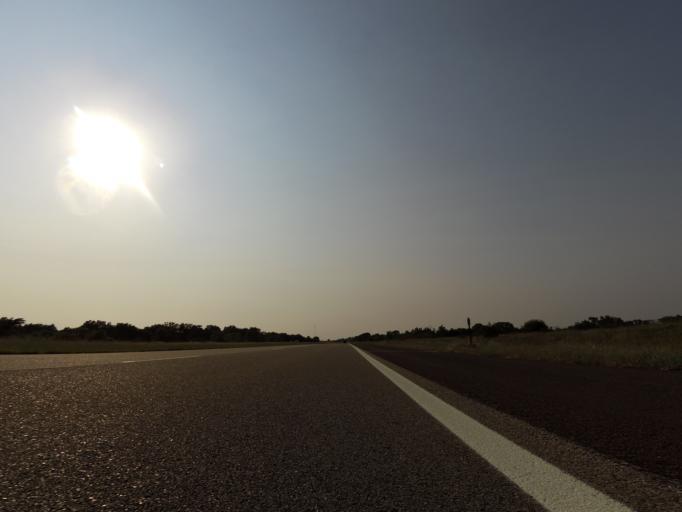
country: US
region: Kansas
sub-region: Reno County
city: South Hutchinson
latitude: 37.9623
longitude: -97.9168
